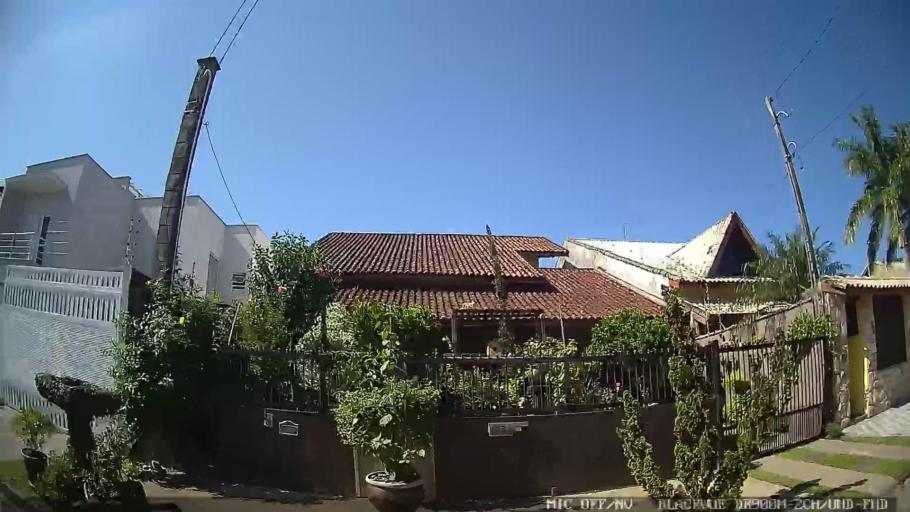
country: BR
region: Sao Paulo
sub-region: Peruibe
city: Peruibe
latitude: -24.2904
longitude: -46.9716
